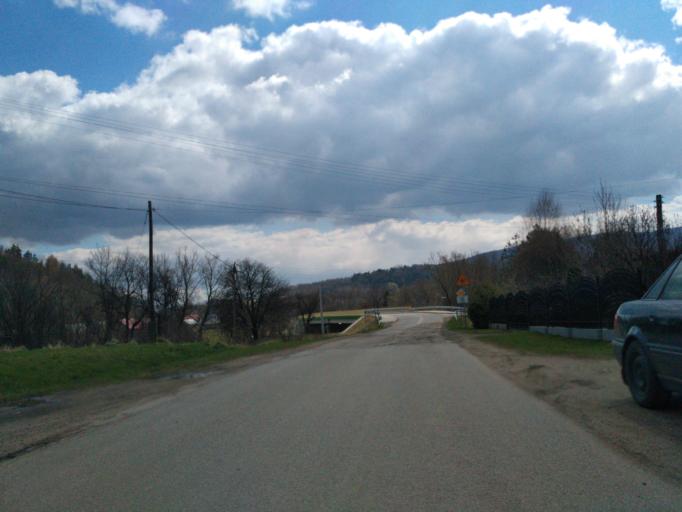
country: PL
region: Subcarpathian Voivodeship
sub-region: Powiat sanocki
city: Tyrawa Woloska
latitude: 49.6104
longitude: 22.2823
